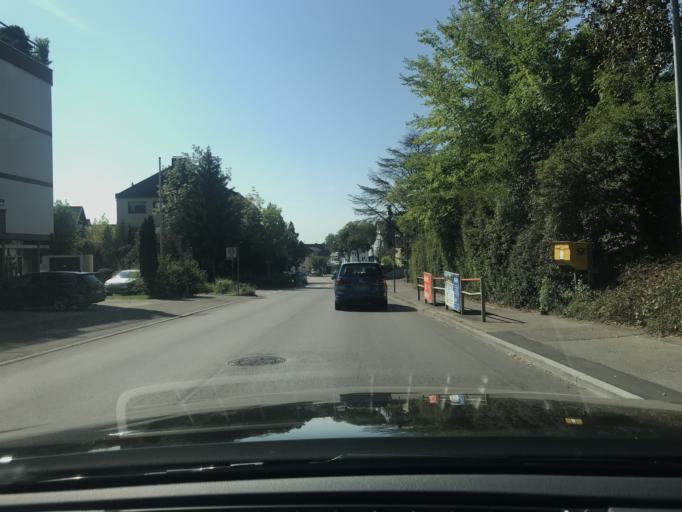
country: DE
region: Baden-Wuerttemberg
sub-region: Regierungsbezirk Stuttgart
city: Ostfildern
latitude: 48.7360
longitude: 9.2135
